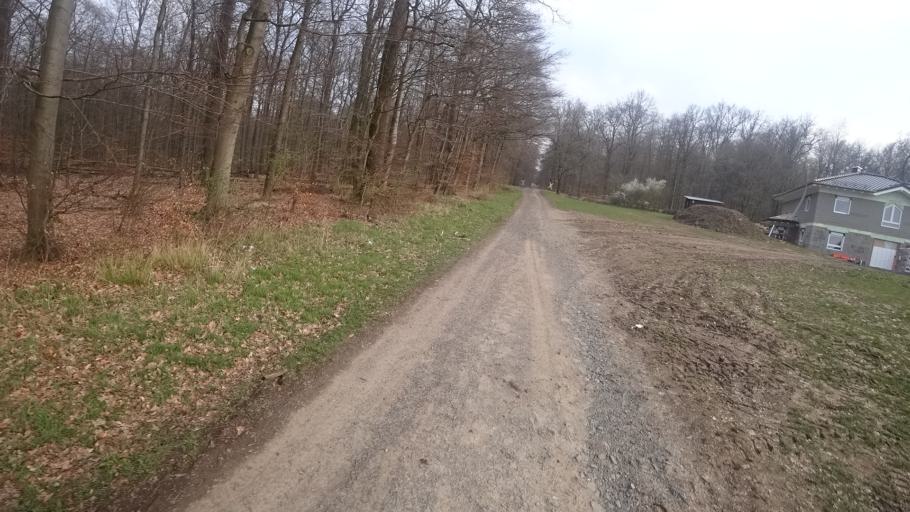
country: DE
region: Rheinland-Pfalz
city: Dickendorf
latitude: 50.7285
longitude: 7.8306
